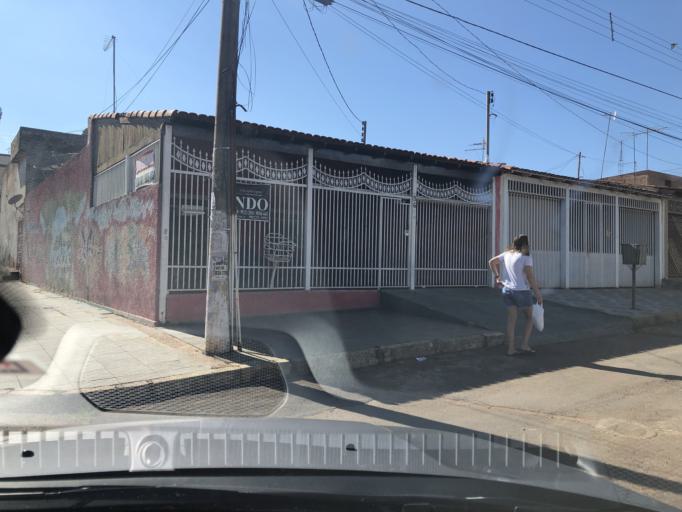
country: BR
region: Federal District
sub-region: Brasilia
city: Brasilia
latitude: -15.7923
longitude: -48.1246
